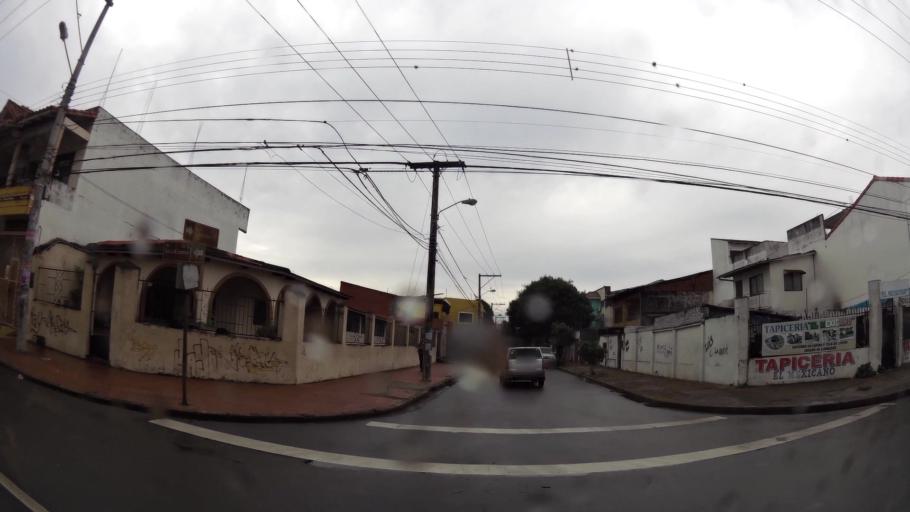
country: BO
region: Santa Cruz
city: Santa Cruz de la Sierra
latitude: -17.7845
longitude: -63.1910
